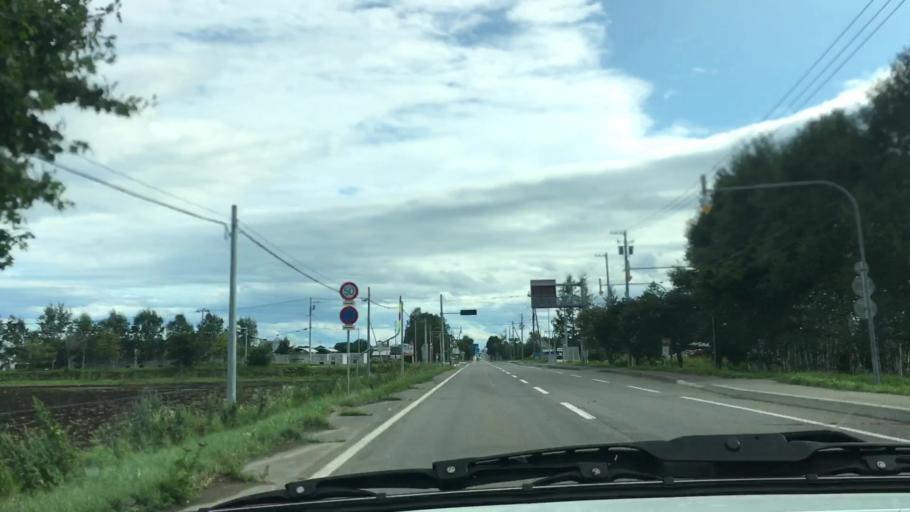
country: JP
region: Hokkaido
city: Otofuke
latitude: 43.2408
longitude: 143.2969
